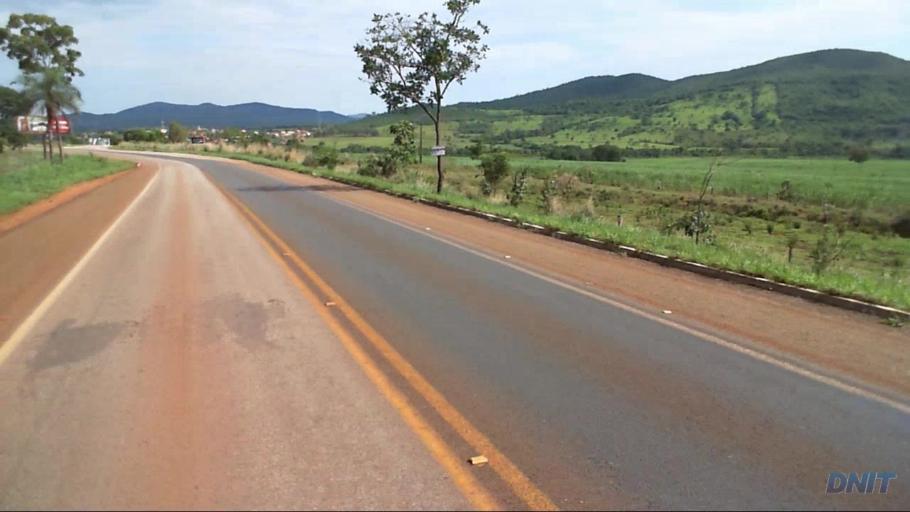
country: BR
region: Goias
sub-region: Barro Alto
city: Barro Alto
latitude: -14.9911
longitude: -48.9084
